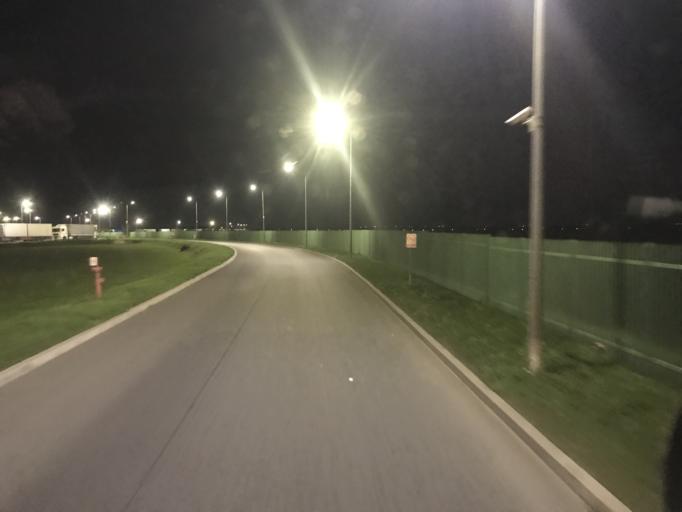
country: PL
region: Lublin Voivodeship
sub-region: Powiat bialski
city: Terespol
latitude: 52.0765
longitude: 23.5207
